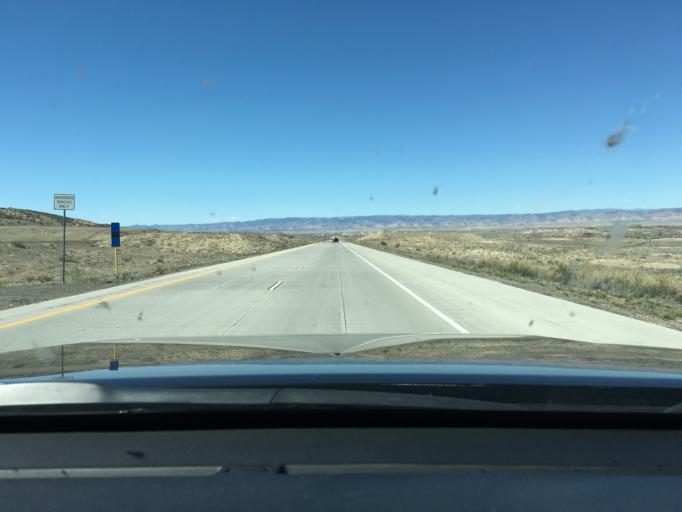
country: US
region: Colorado
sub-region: Mesa County
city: Loma
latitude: 39.2067
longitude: -108.8581
